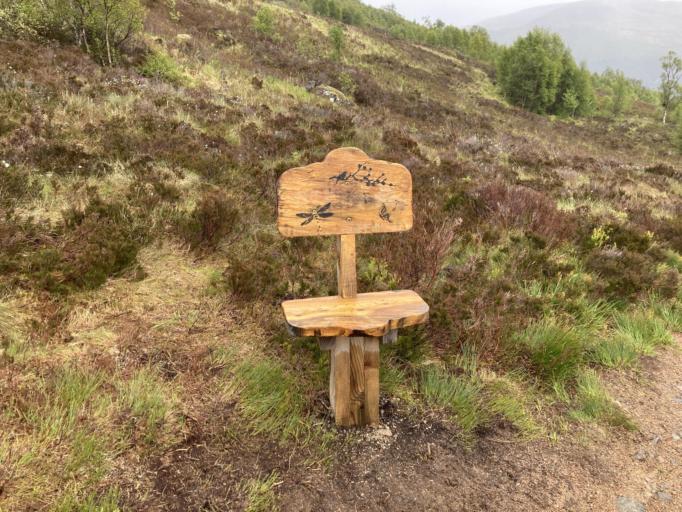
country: GB
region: Scotland
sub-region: Highland
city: Spean Bridge
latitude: 56.9645
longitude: -4.5176
